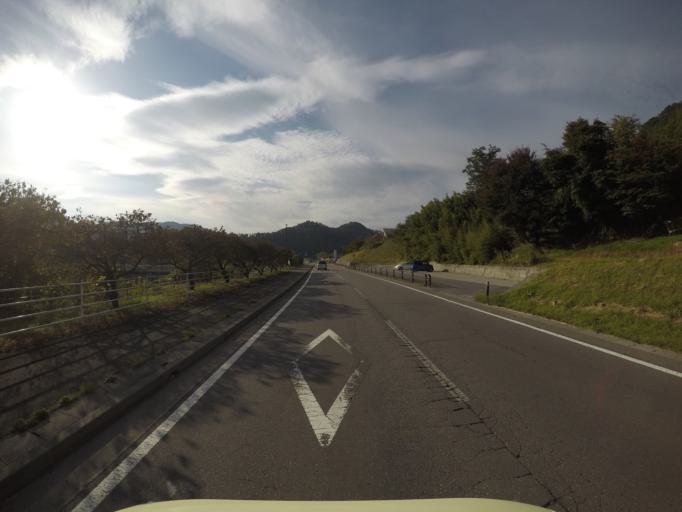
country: JP
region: Nagano
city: Kamimaruko
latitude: 36.3279
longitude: 138.2642
